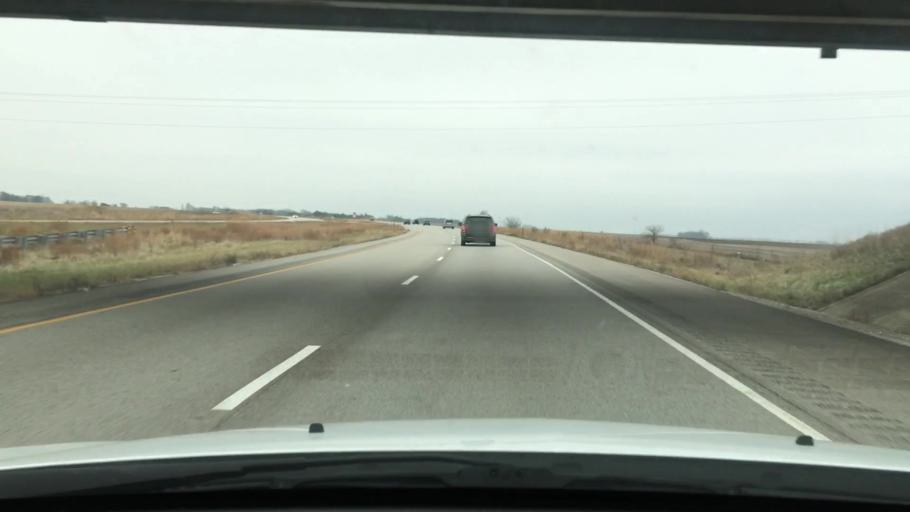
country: US
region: Illinois
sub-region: Sangamon County
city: New Berlin
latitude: 39.7369
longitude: -89.9849
